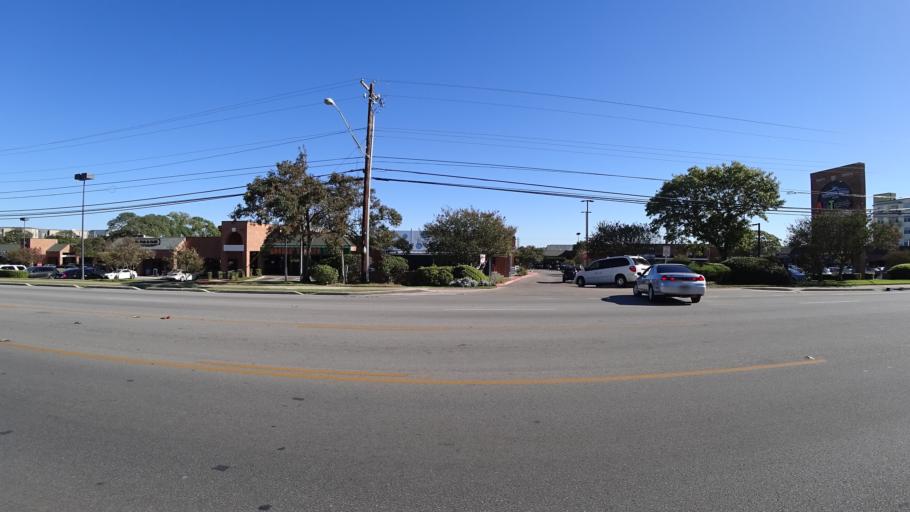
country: US
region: Texas
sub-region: Travis County
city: Rollingwood
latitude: 30.2425
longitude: -97.7838
